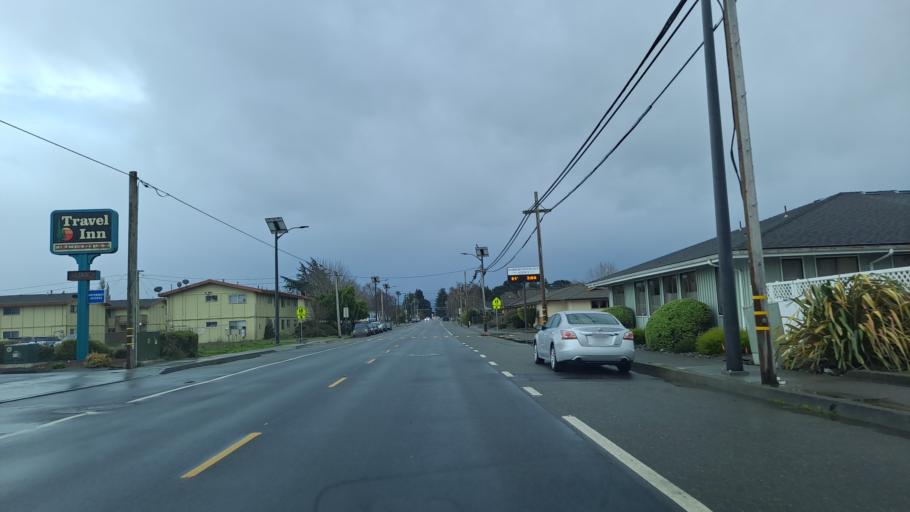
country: US
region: California
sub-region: Humboldt County
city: Fortuna
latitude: 40.5933
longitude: -124.1545
